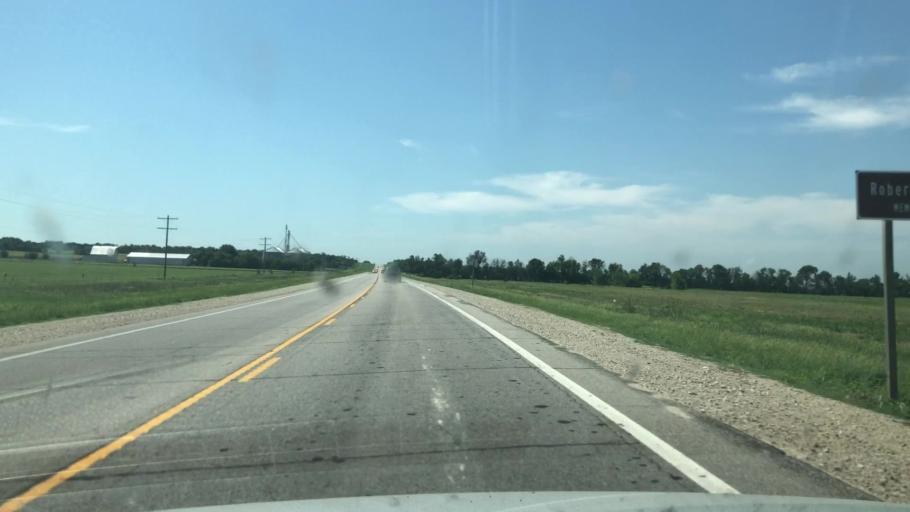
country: US
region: Kansas
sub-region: Butler County
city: Douglass
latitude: 37.3865
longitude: -97.0069
